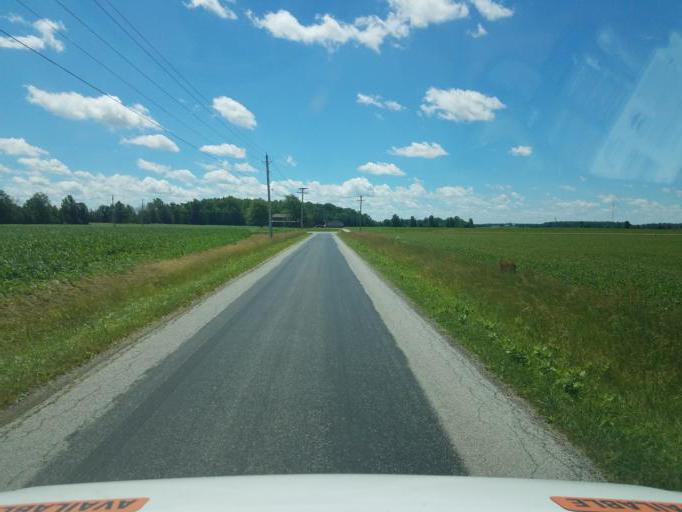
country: US
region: Ohio
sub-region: Crawford County
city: Galion
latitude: 40.7346
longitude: -82.8721
